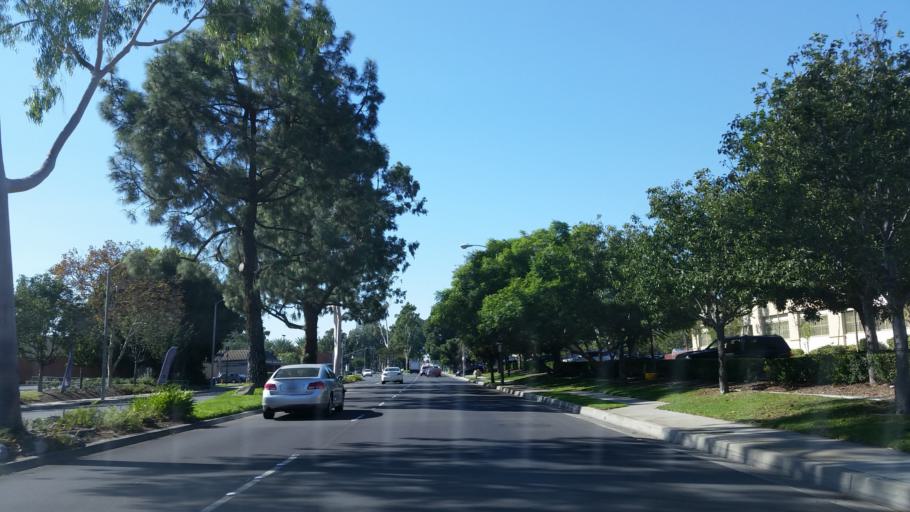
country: US
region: California
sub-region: Los Angeles County
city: Artesia
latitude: 33.8585
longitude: -118.0866
